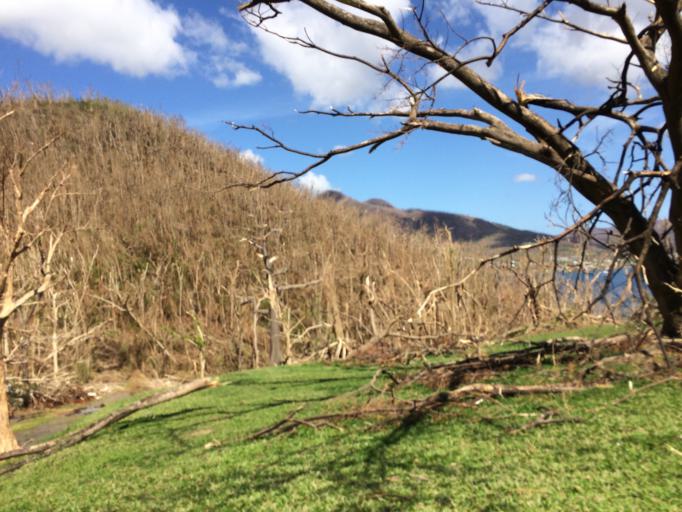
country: DM
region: Saint John
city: Portsmouth
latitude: 15.5836
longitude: -61.4733
